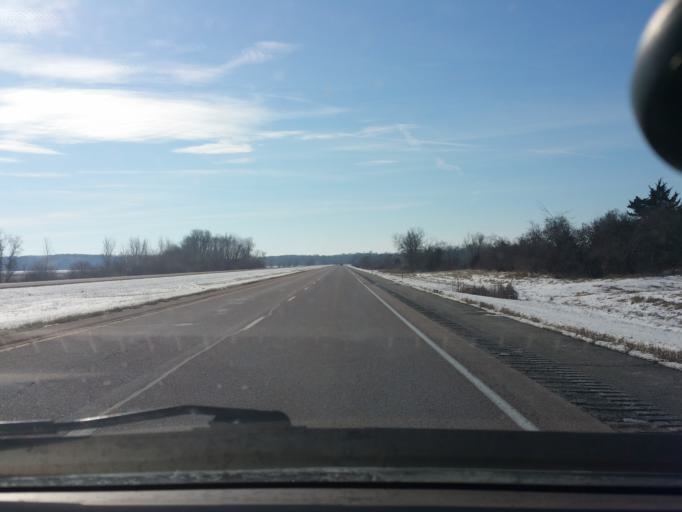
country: US
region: Iowa
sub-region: Decatur County
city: Lamoni
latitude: 40.6792
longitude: -93.8485
